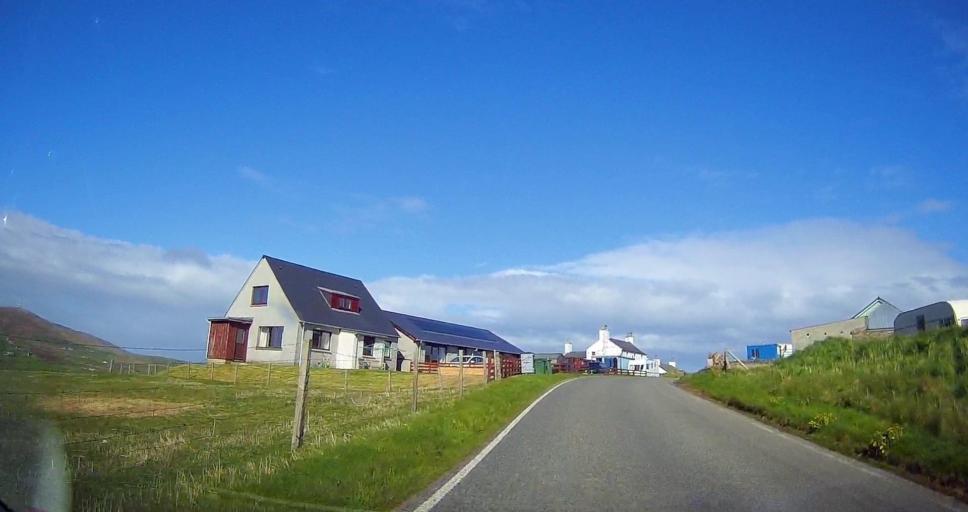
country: GB
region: Scotland
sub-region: Shetland Islands
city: Sandwick
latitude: 59.9166
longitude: -1.3190
